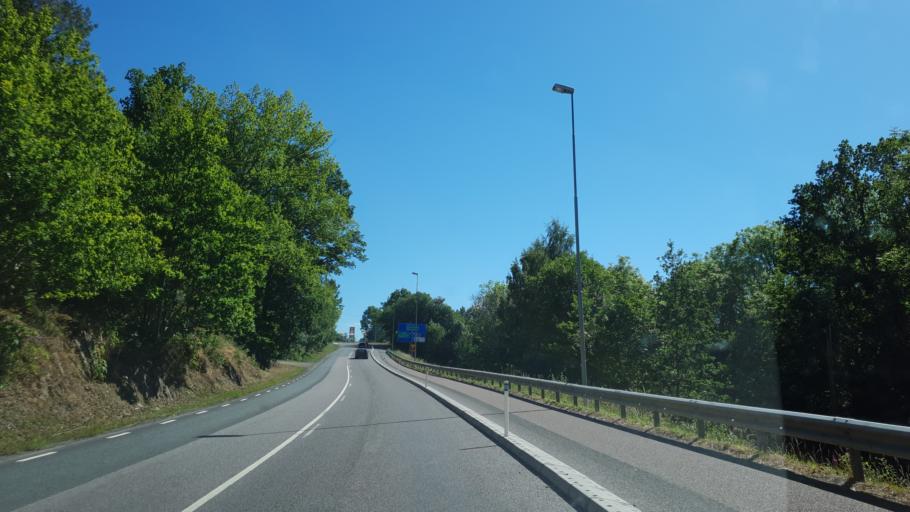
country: SE
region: Joenkoeping
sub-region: Jonkopings Kommun
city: Graenna
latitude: 58.0058
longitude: 14.4529
